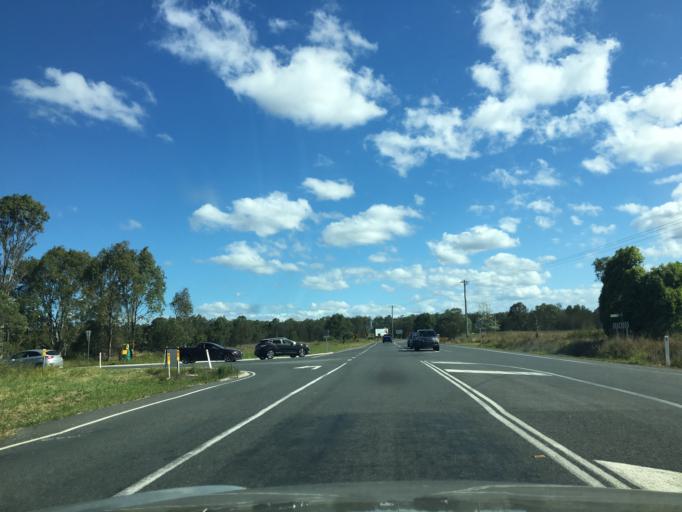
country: AU
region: Queensland
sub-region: Logan
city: Logan Reserve
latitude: -27.7495
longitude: 153.1255
